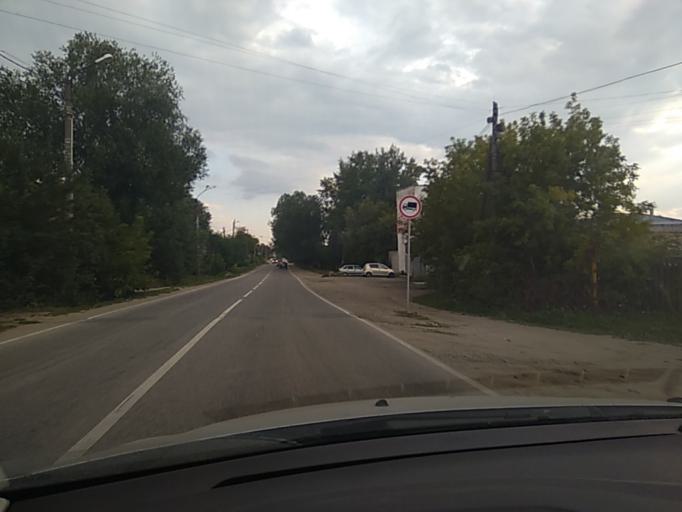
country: RU
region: Chelyabinsk
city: Kyshtym
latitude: 55.7000
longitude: 60.5527
